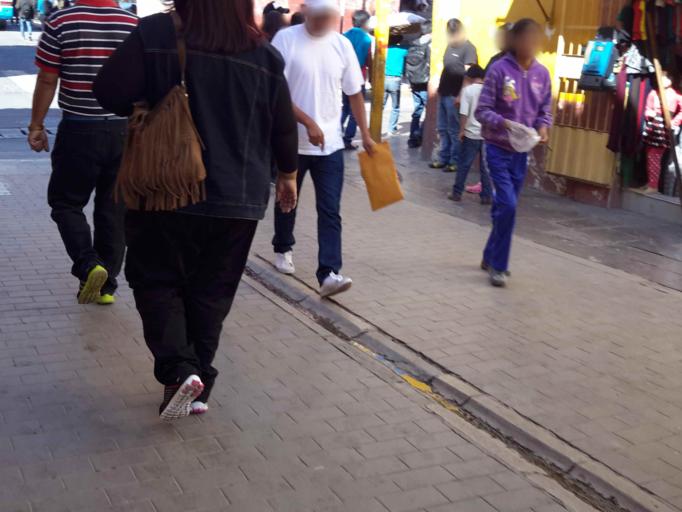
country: PE
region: Ayacucho
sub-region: Provincia de Huamanga
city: Ayacucho
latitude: -13.1630
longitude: -74.2270
